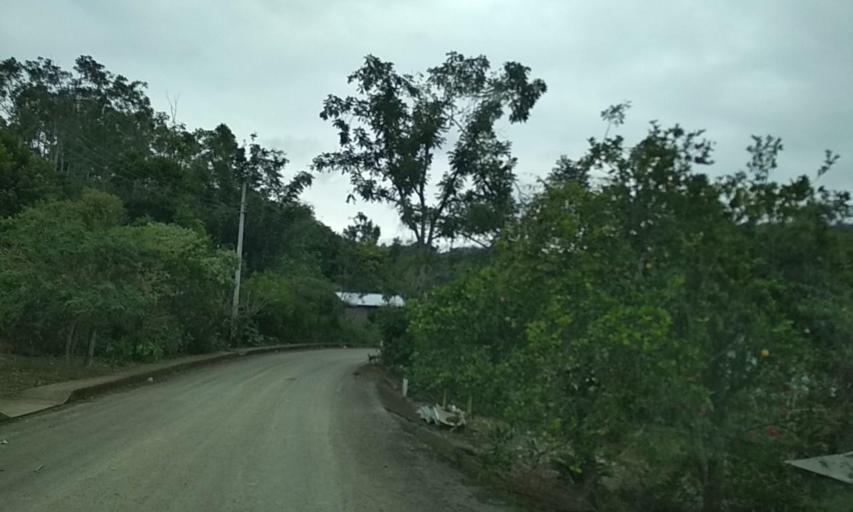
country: MX
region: Veracruz
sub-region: Coatzintla
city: Manuel Maria Contreras
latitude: 20.3598
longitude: -97.5104
